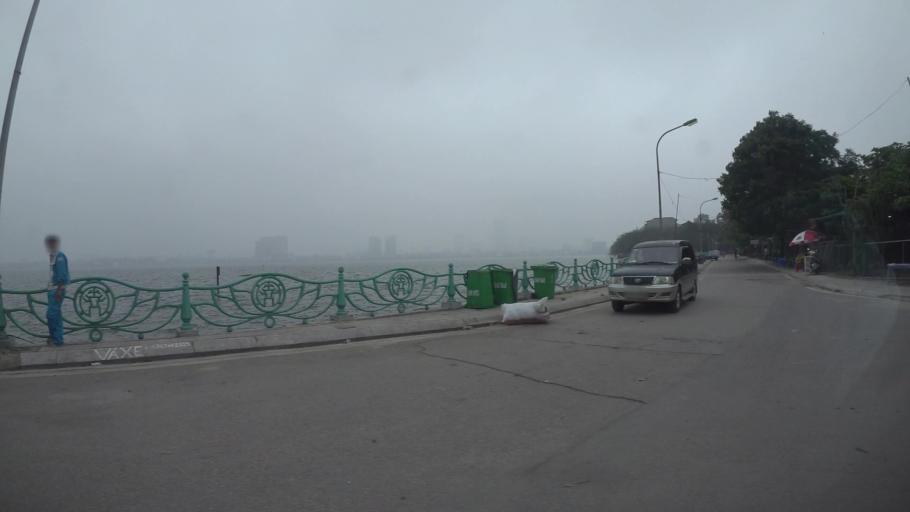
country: VN
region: Ha Noi
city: Tay Ho
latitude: 21.0571
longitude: 105.8231
